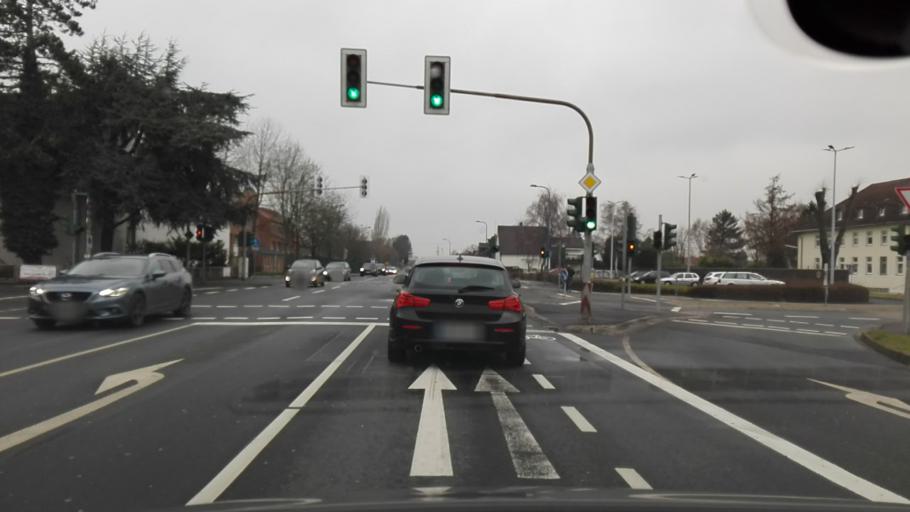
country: DE
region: North Rhine-Westphalia
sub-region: Regierungsbezirk Arnsberg
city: Unna
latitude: 51.5634
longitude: 7.6794
